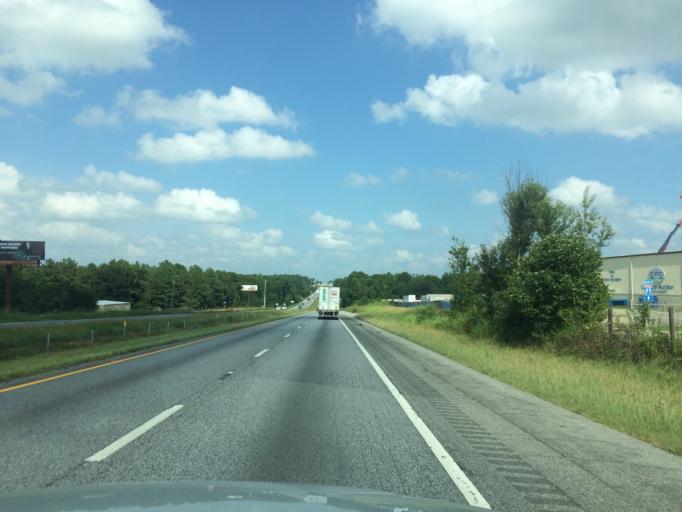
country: US
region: South Carolina
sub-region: Spartanburg County
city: Cowpens
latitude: 35.0460
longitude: -81.8115
